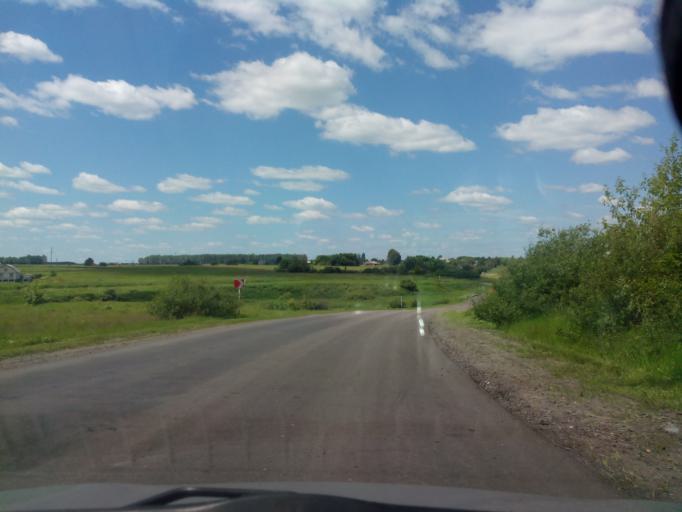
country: RU
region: Voronezj
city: Ternovka
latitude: 51.6677
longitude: 41.6449
